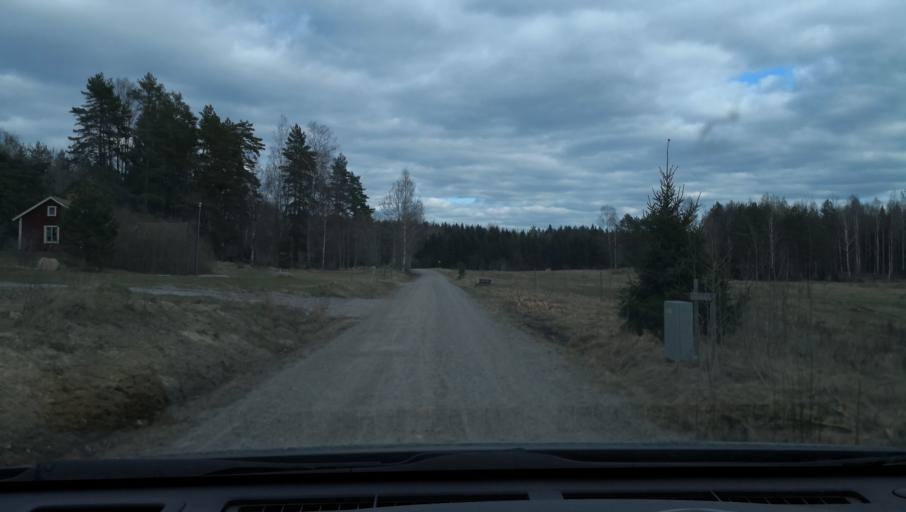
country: SE
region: Soedermanland
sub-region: Katrineholms Kommun
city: Katrineholm
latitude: 59.1314
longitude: 16.1742
